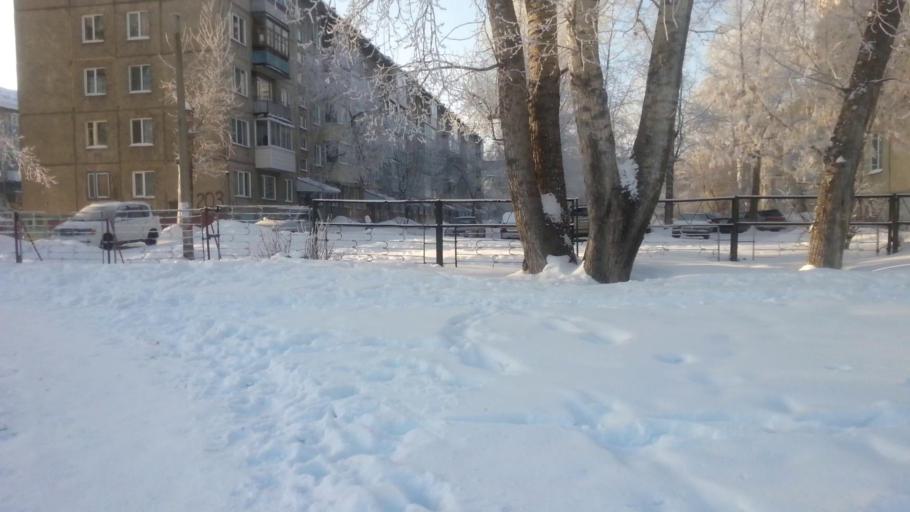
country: RU
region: Altai Krai
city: Novosilikatnyy
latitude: 53.3763
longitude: 83.6734
